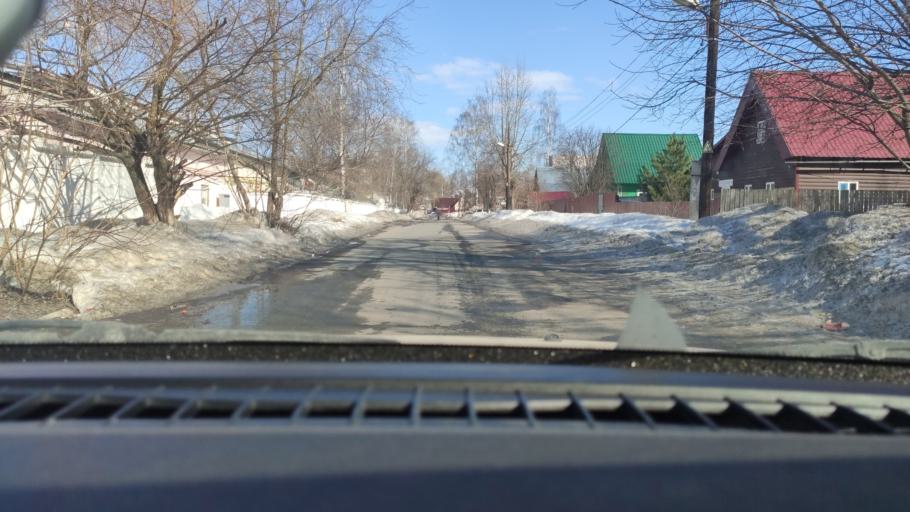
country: RU
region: Perm
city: Polazna
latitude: 58.1288
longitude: 56.3861
